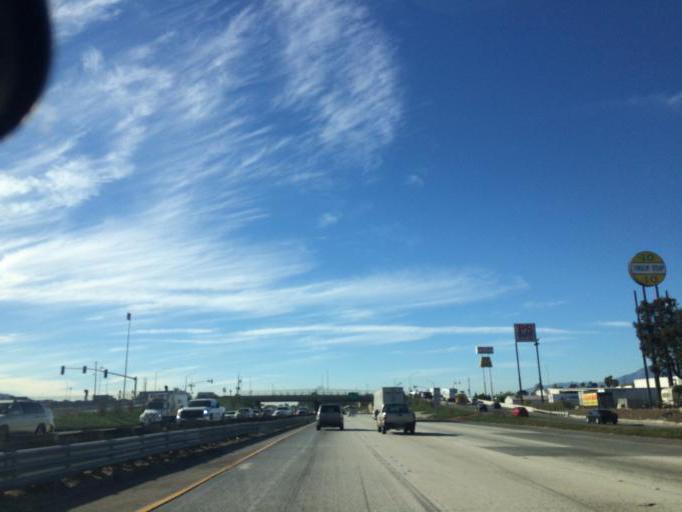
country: US
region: California
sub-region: San Bernardino County
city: Bloomington
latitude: 34.0689
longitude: -117.3671
